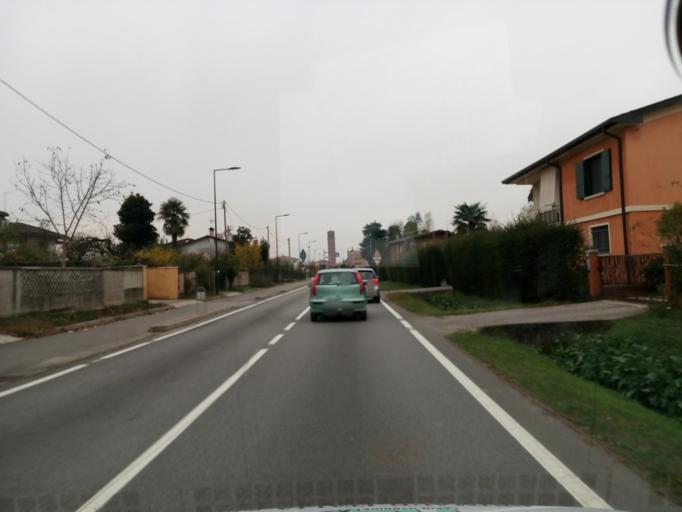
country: IT
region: Veneto
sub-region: Provincia di Padova
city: Piombino Dese
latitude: 45.6123
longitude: 12.0046
